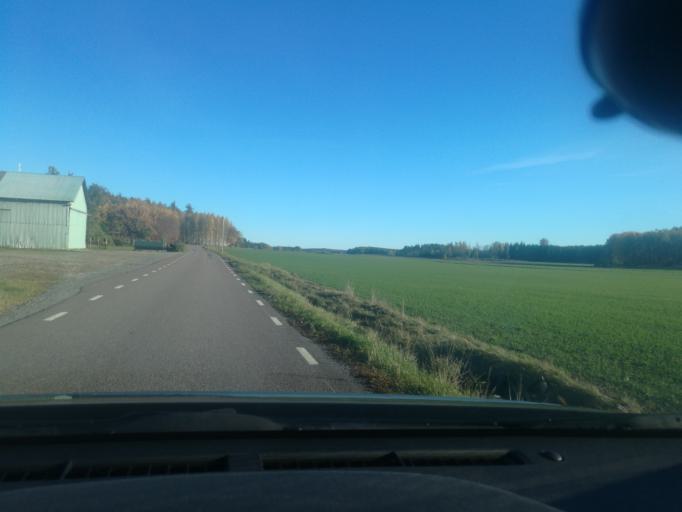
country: SE
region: Vaestmanland
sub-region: Kopings Kommun
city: Koping
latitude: 59.5780
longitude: 16.0041
